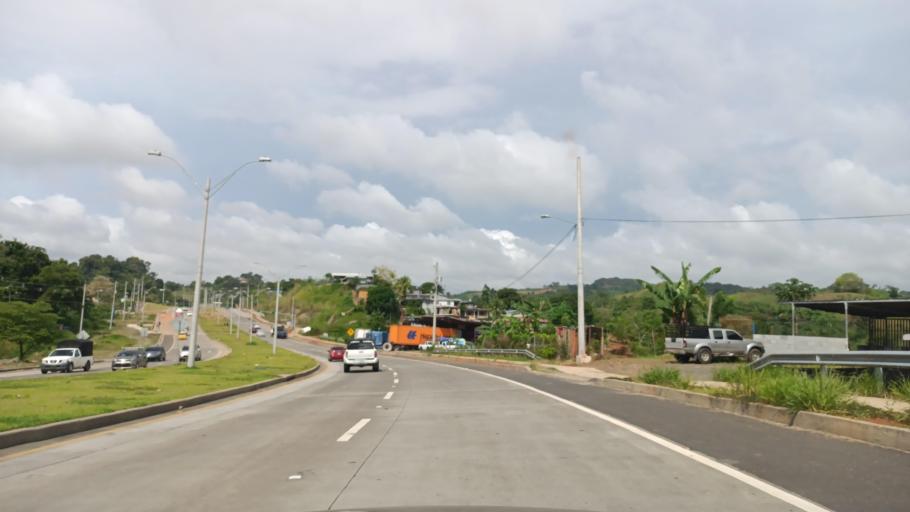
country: PA
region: Panama
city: Las Cumbres
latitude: 9.0995
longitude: -79.4886
